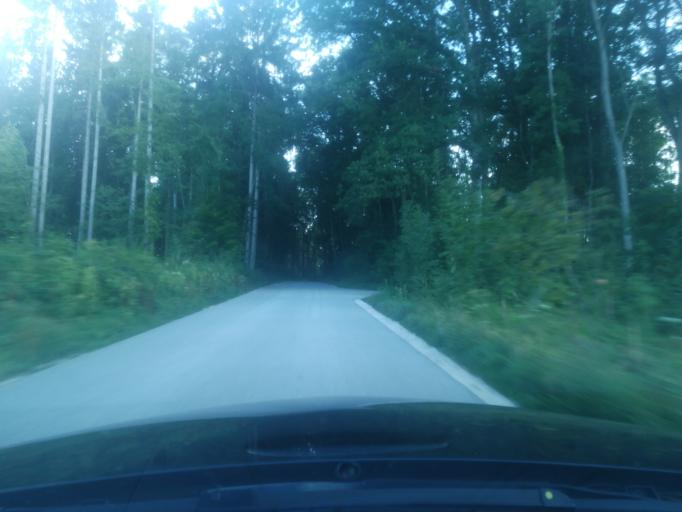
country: AT
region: Upper Austria
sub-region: Wels-Land
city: Marchtrenk
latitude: 48.1618
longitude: 14.1680
